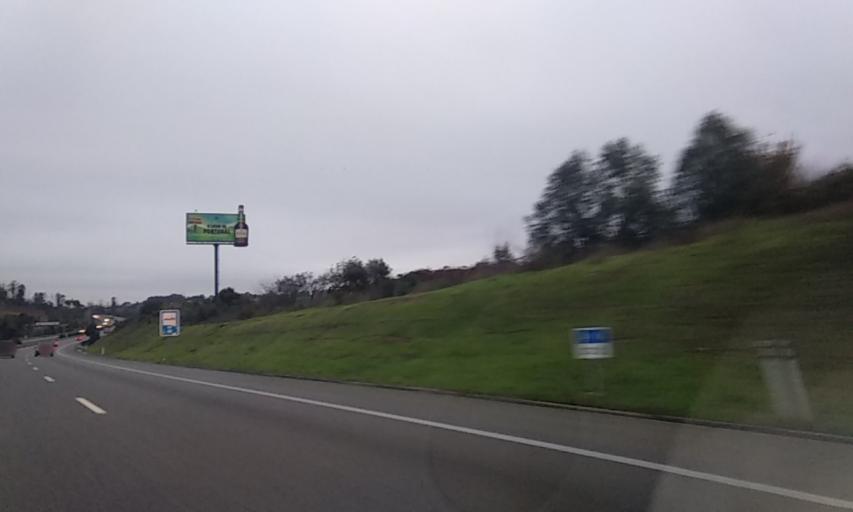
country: PT
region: Aveiro
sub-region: Mealhada
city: Mealhada
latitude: 40.3983
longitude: -8.4906
